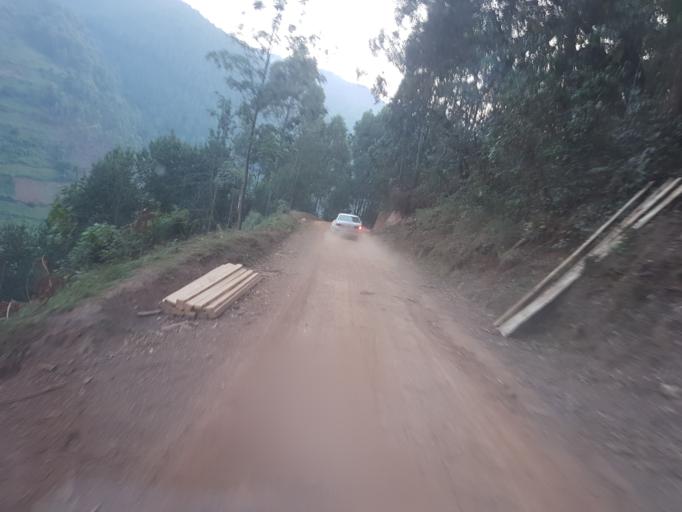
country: UG
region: Western Region
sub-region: Kanungu District
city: Kanungu
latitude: -0.9588
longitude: 29.8345
